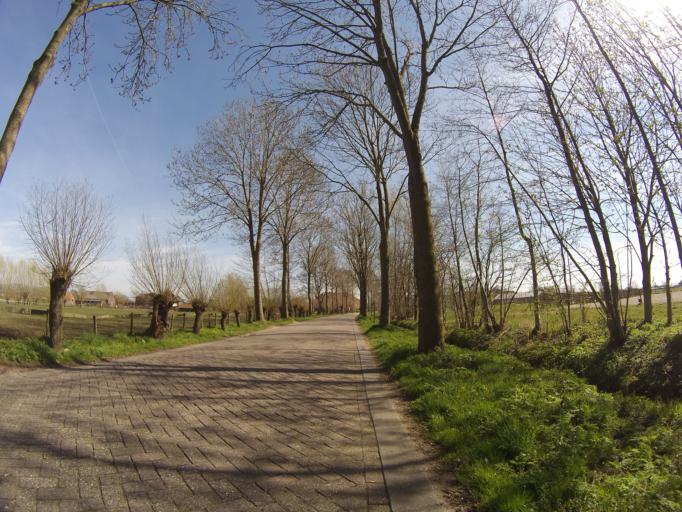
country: NL
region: Gelderland
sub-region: Gemeente Nijkerk
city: Nijkerk
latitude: 52.2081
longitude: 5.4886
